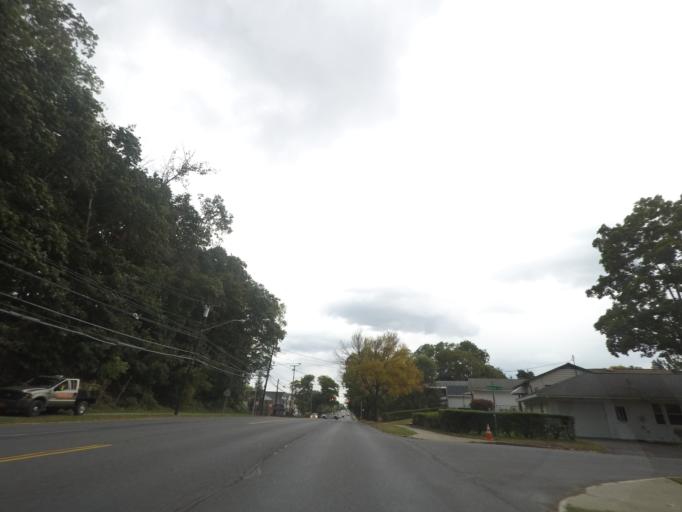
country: US
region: New York
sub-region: Albany County
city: Roessleville
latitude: 42.6735
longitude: -73.8140
